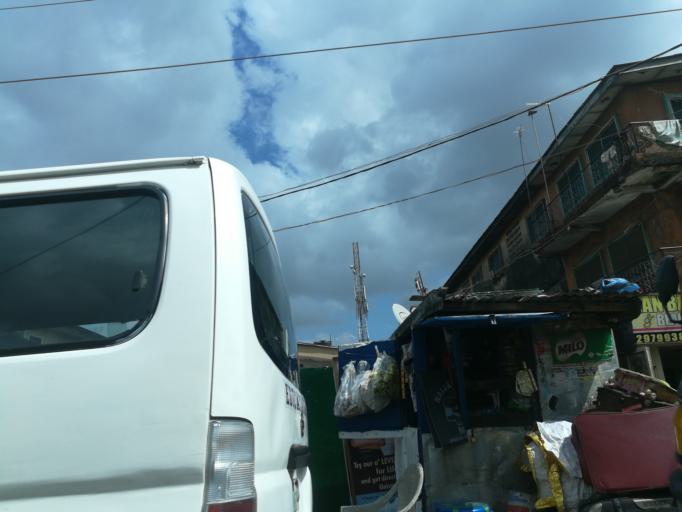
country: NG
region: Lagos
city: Mushin
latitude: 6.5401
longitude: 3.3598
